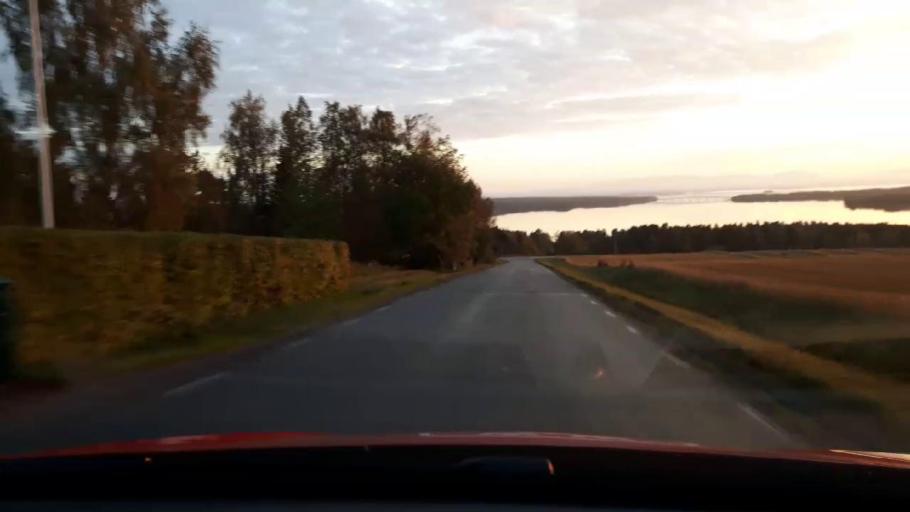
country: SE
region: Jaemtland
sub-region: OEstersunds Kommun
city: Ostersund
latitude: 63.2447
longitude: 14.5466
